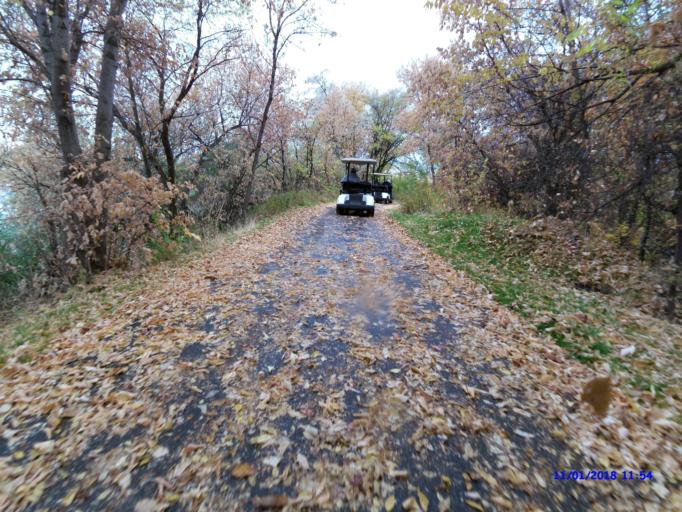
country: US
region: Utah
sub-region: Weber County
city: Ogden
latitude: 41.2326
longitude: -111.9923
